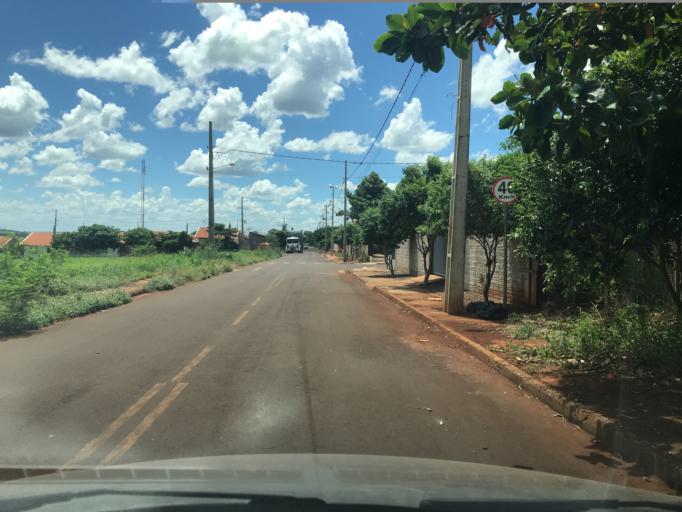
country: BR
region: Parana
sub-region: Palotina
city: Palotina
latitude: -24.2684
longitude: -53.8475
